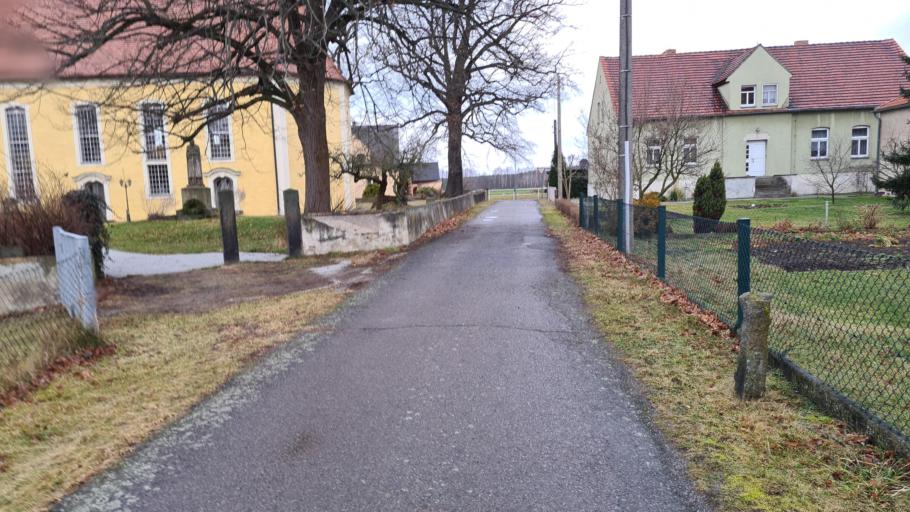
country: DE
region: Brandenburg
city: Kroppen
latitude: 51.3850
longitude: 13.8002
